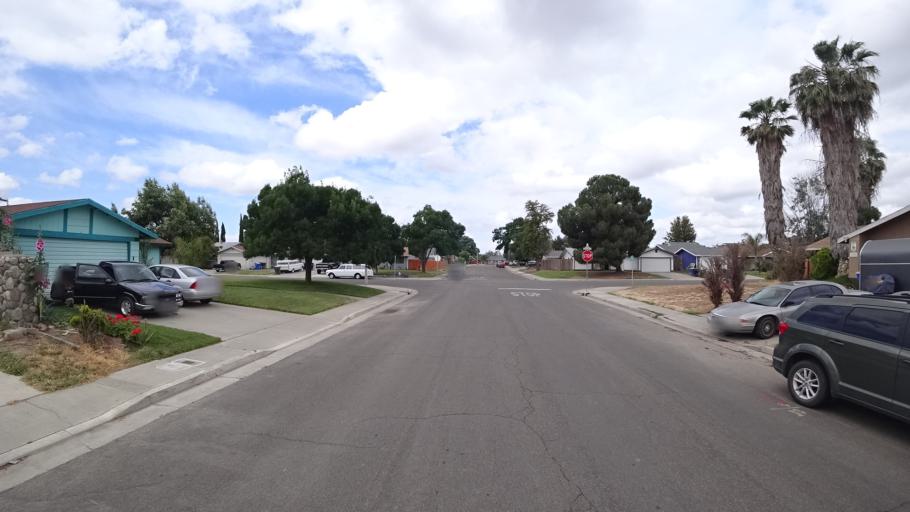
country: US
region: California
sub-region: Kings County
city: Hanford
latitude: 36.3114
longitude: -119.6631
